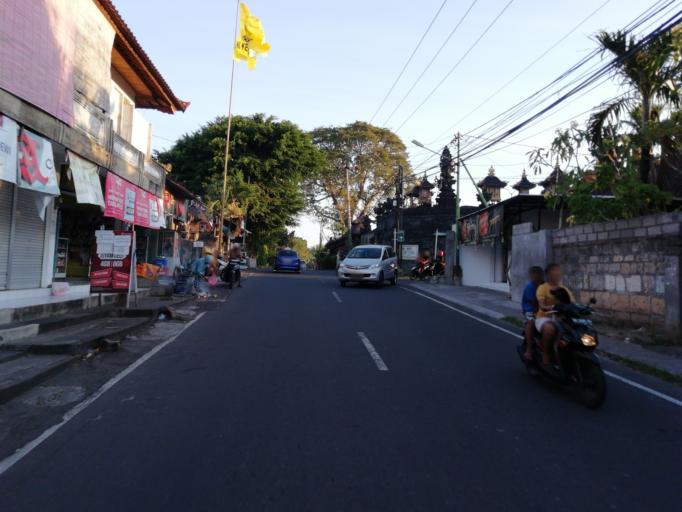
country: ID
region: Bali
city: Jimbaran
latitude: -8.8289
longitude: 115.1654
